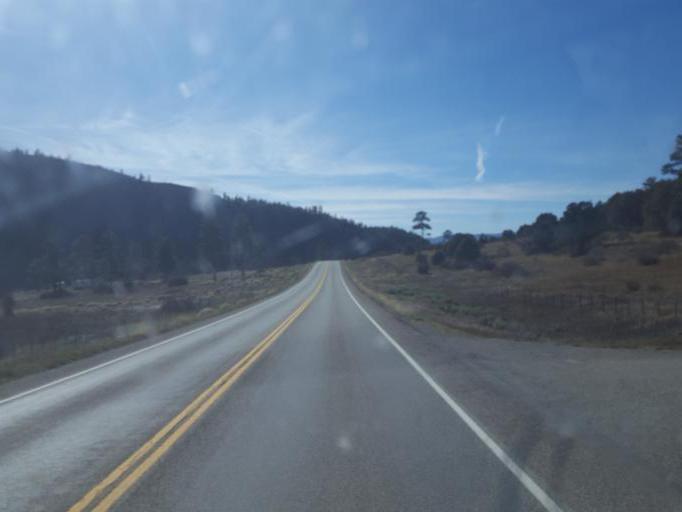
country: US
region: Colorado
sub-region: Archuleta County
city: Pagosa Springs
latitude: 37.2153
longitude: -107.2274
